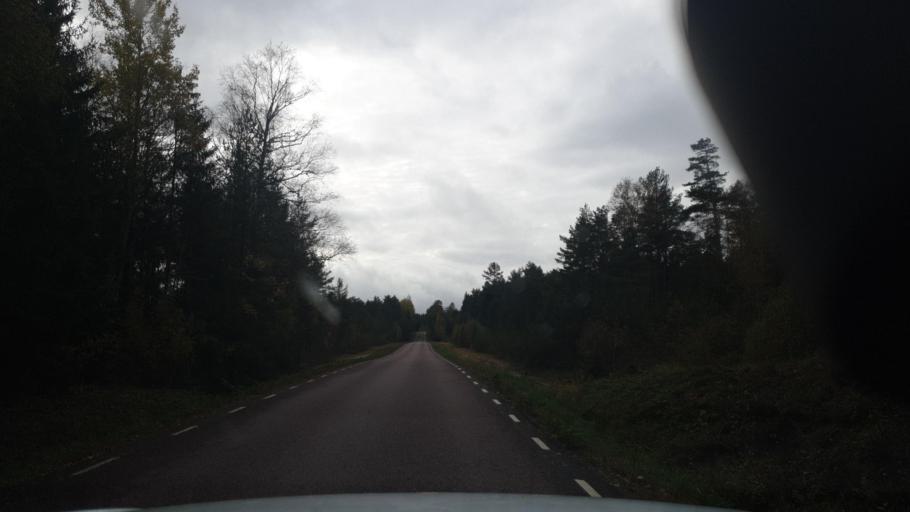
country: SE
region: Vaermland
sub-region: Karlstads Kommun
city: Edsvalla
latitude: 59.5197
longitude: 13.1118
